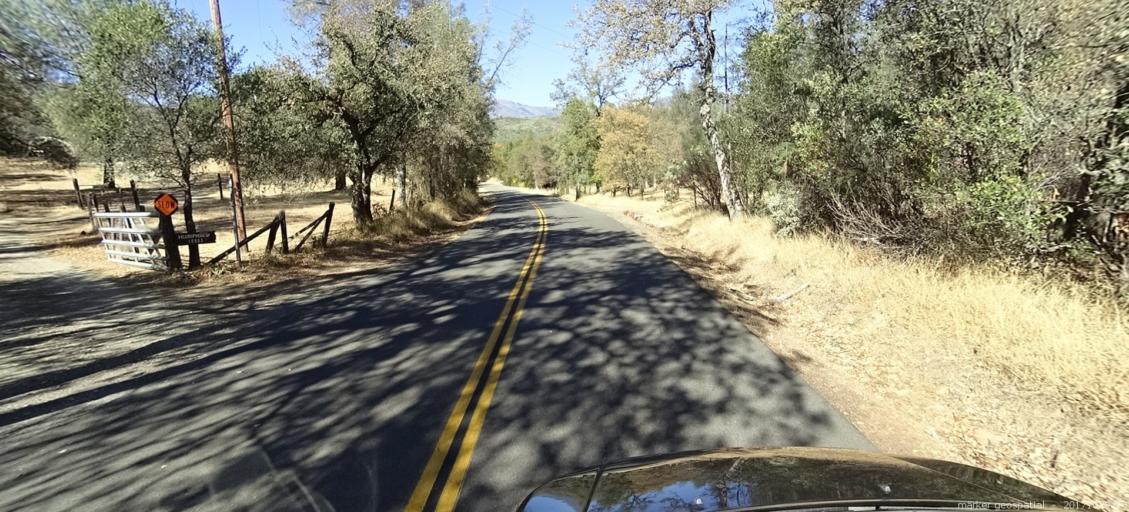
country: US
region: California
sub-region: Shasta County
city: Shasta
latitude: 40.4800
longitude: -122.6522
